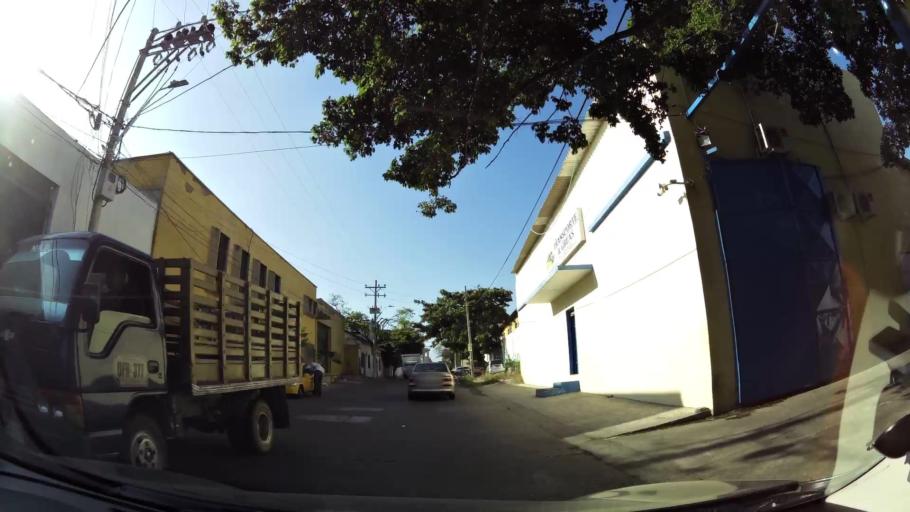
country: CO
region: Atlantico
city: Barranquilla
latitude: 10.9881
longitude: -74.7822
